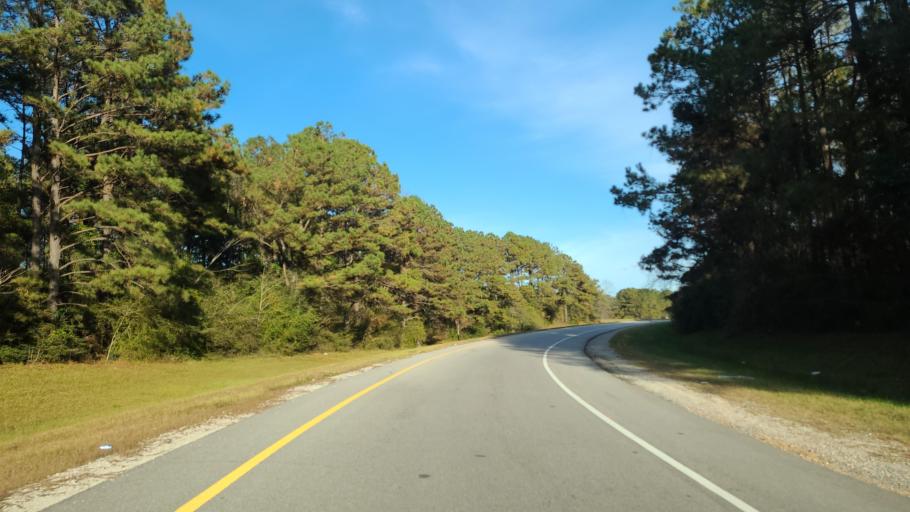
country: US
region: Mississippi
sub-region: Forrest County
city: Hattiesburg
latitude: 31.2382
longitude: -89.3211
